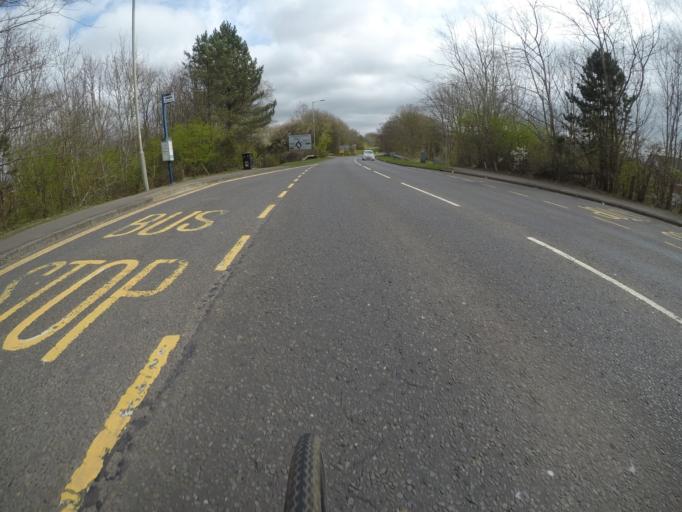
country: GB
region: Scotland
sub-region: North Ayrshire
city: Irvine
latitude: 55.6221
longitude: -4.6444
